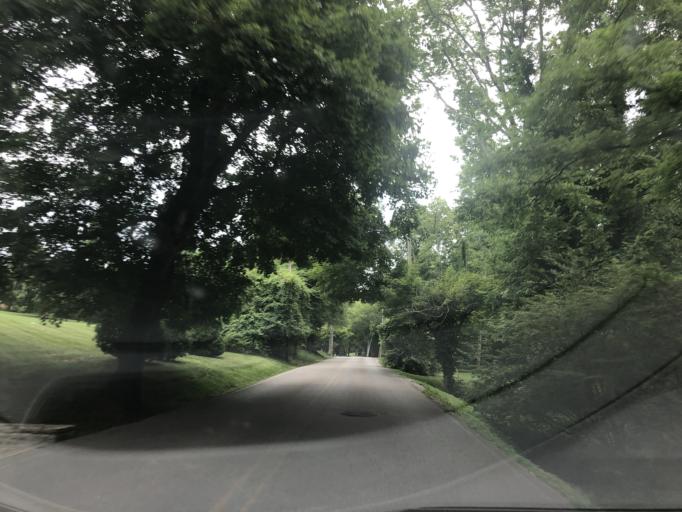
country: US
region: Tennessee
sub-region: Davidson County
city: Oak Hill
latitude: 36.0930
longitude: -86.7783
